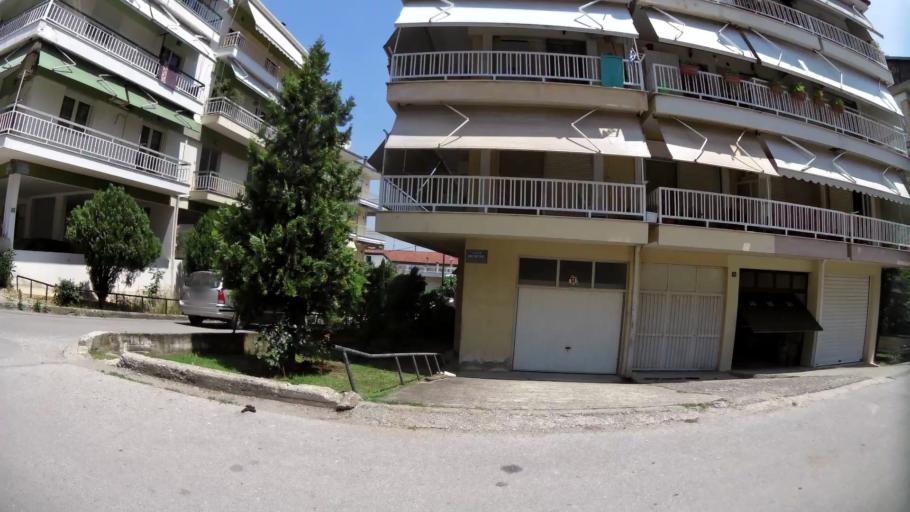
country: GR
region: Central Macedonia
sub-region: Nomos Imathias
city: Veroia
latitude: 40.5116
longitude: 22.2051
